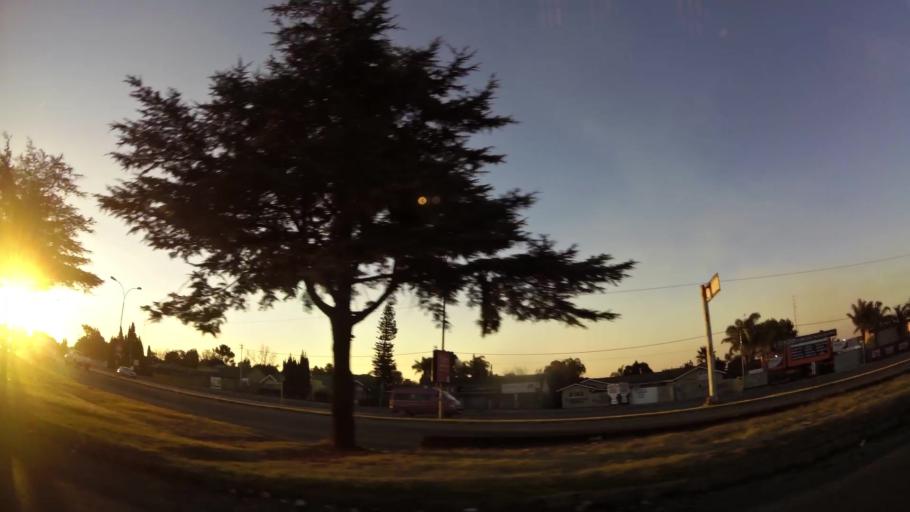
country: ZA
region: Gauteng
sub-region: City of Johannesburg Metropolitan Municipality
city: Roodepoort
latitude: -26.1461
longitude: 27.8828
